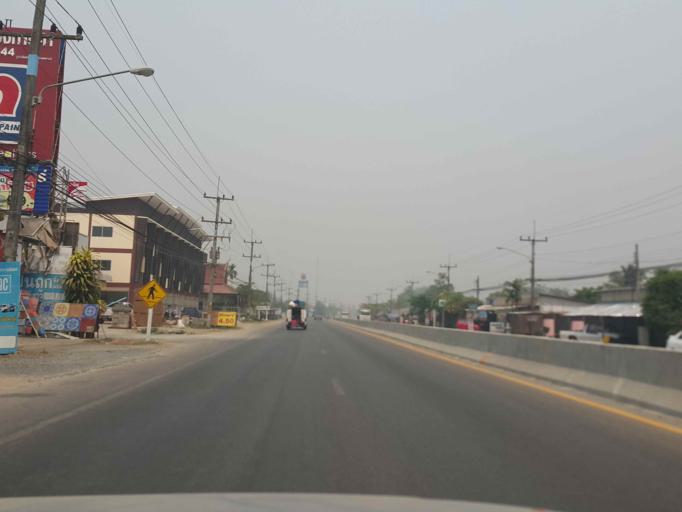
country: TH
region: Chiang Mai
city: Mae Taeng
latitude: 19.0789
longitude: 98.9375
